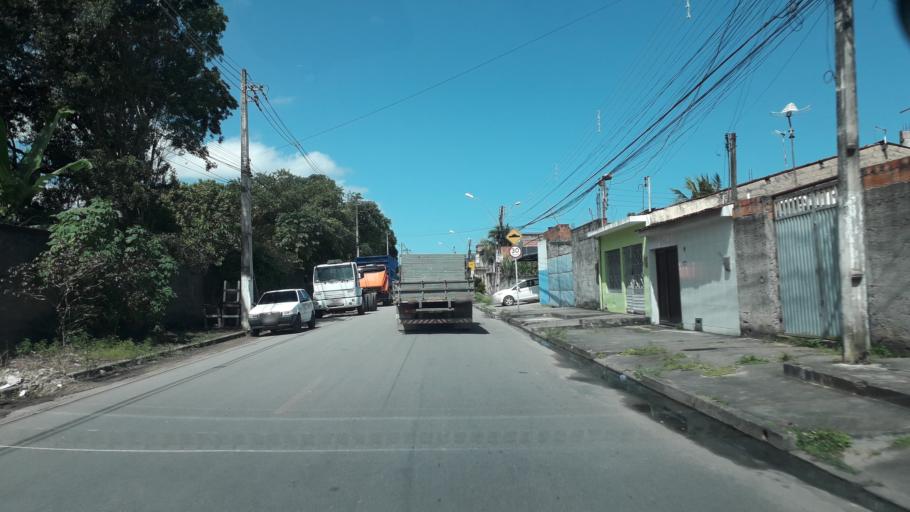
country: BR
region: Alagoas
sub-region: Satuba
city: Satuba
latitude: -9.5590
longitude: -35.7831
